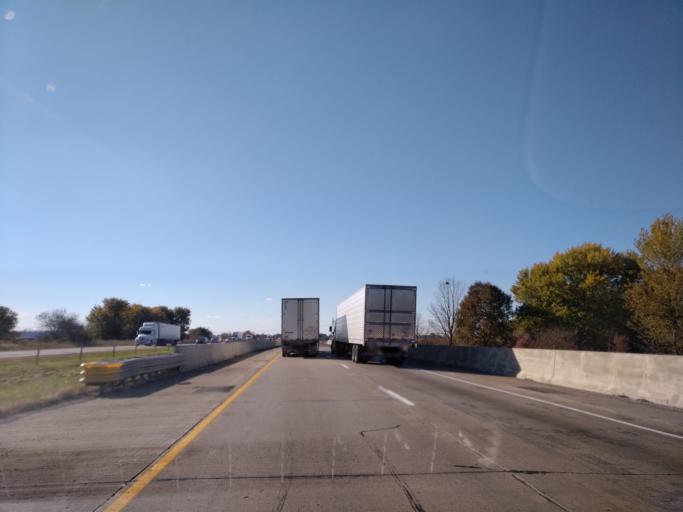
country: US
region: Indiana
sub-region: Hancock County
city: Greenfield
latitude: 39.8258
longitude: -85.6668
